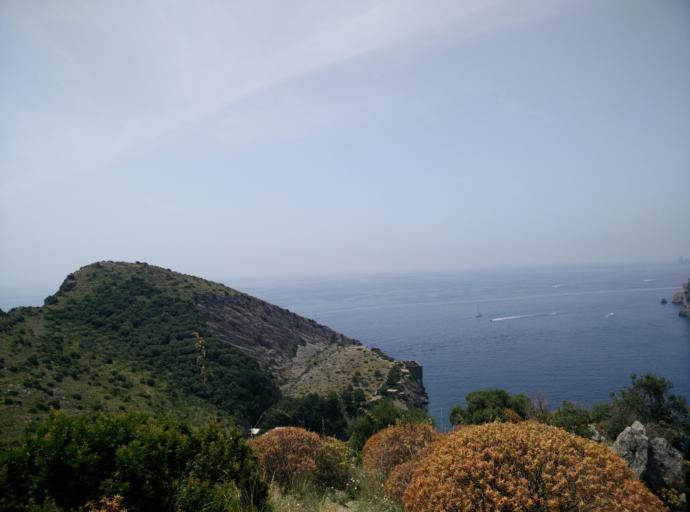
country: IT
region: Campania
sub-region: Provincia di Napoli
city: Massa Lubrense
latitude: 40.5765
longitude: 14.3423
